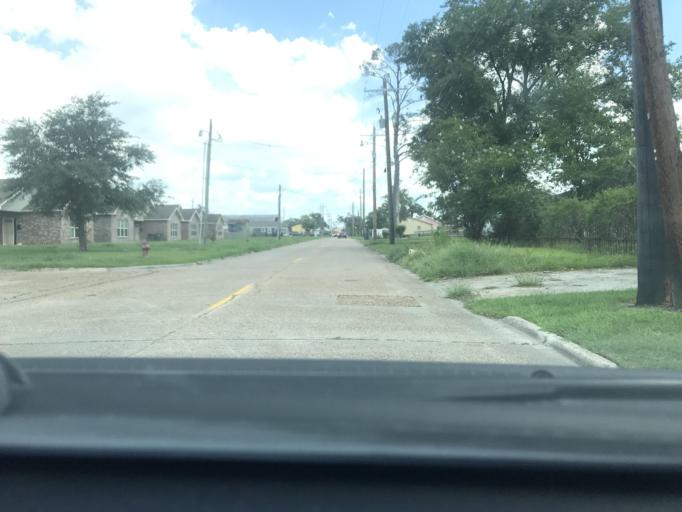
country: US
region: Louisiana
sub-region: Calcasieu Parish
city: Lake Charles
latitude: 30.2080
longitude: -93.2160
